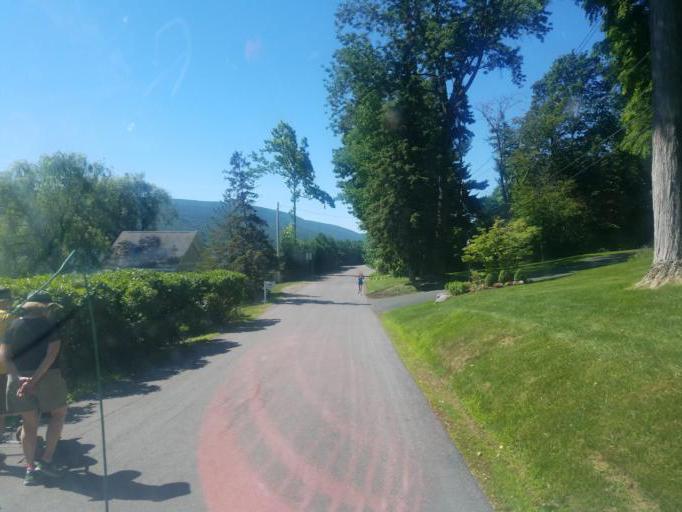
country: US
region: New York
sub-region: Ontario County
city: Naples
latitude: 42.7302
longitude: -77.3514
